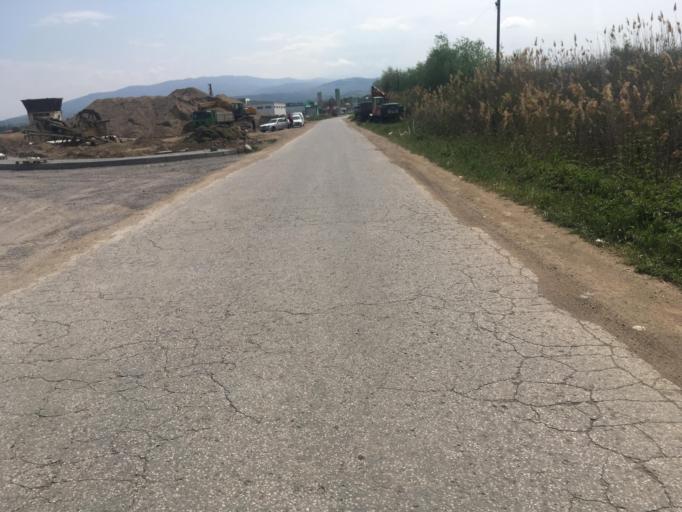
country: MK
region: Karbinci
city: Karbinci
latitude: 41.8005
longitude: 22.2160
